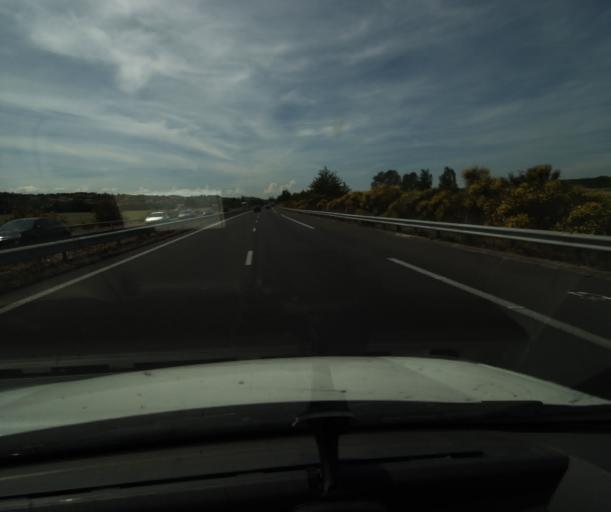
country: FR
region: Languedoc-Roussillon
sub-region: Departement de l'Aude
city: Villeneuve-la-Comptal
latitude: 43.3127
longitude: 1.8912
